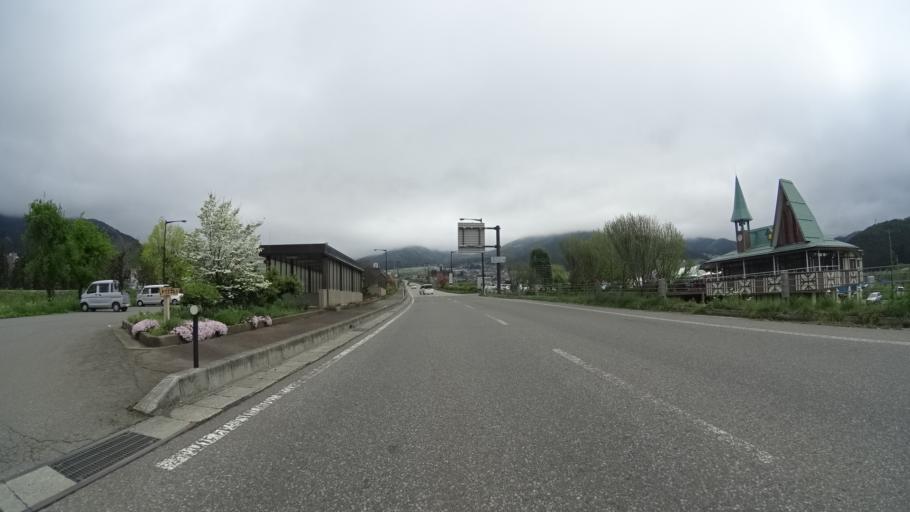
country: JP
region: Nagano
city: Nakano
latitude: 36.7419
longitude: 138.4047
